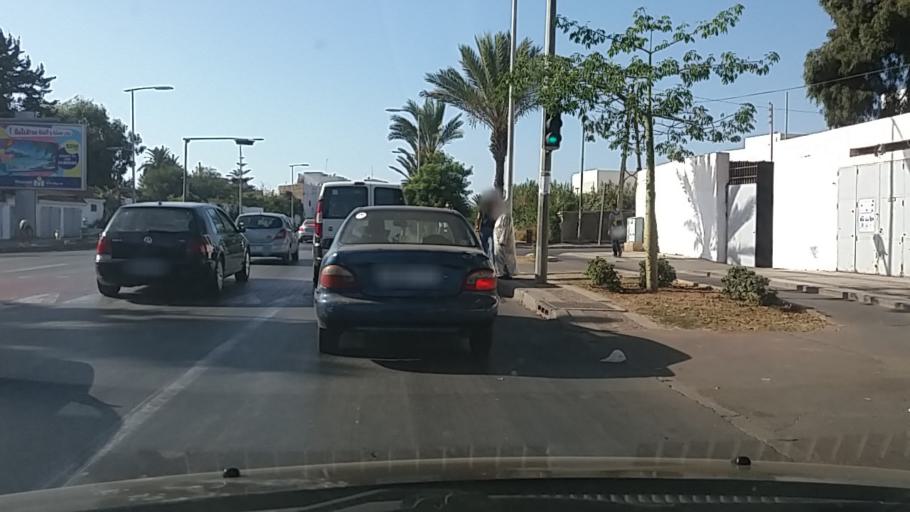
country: MA
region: Rabat-Sale-Zemmour-Zaer
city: Sale
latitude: 34.0434
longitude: -6.8174
